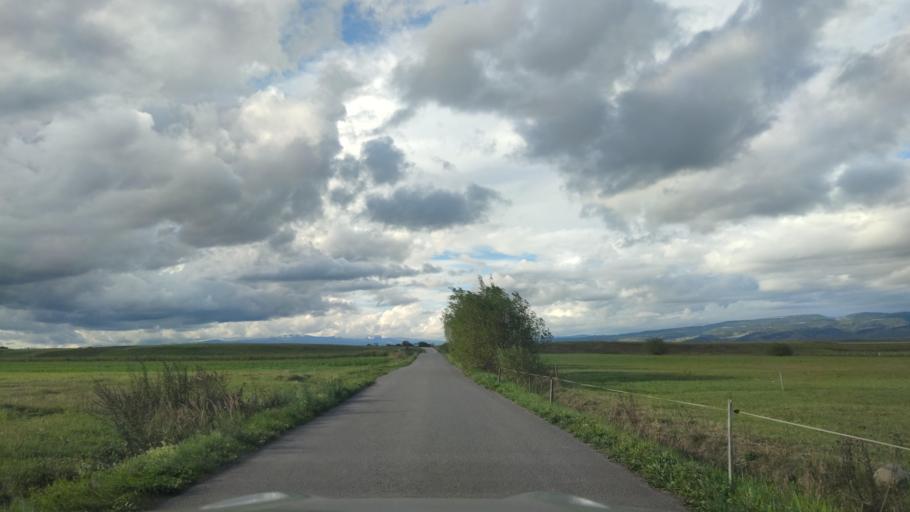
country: RO
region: Harghita
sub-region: Comuna Remetea
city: Remetea
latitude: 46.8120
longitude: 25.4360
